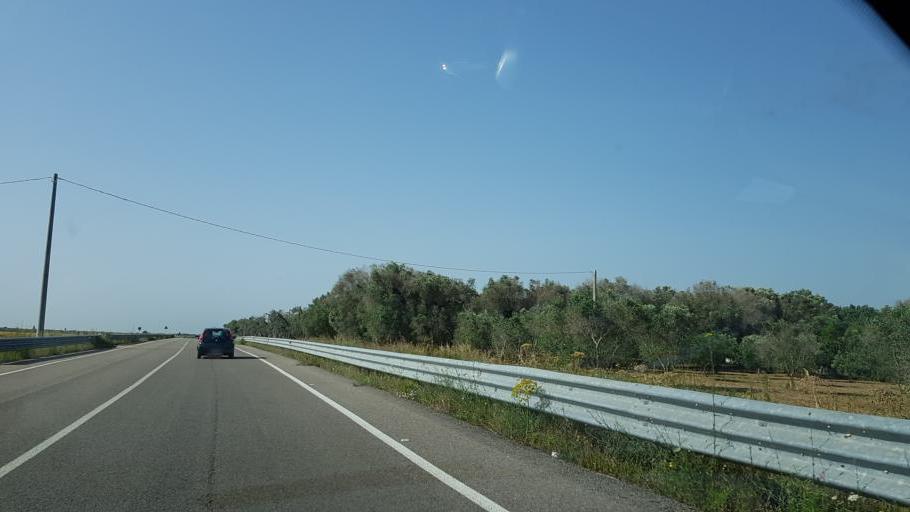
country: IT
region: Apulia
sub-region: Provincia di Brindisi
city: Mesagne
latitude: 40.5070
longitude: 17.8273
